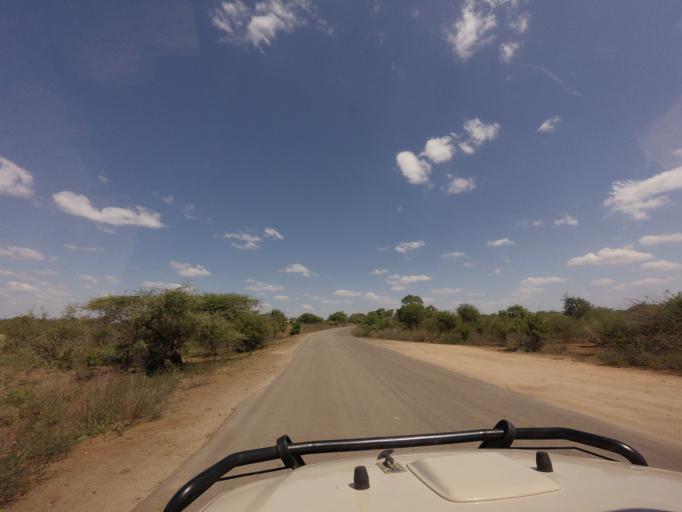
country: ZA
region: Mpumalanga
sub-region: Ehlanzeni District
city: Komatipoort
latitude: -25.1166
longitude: 31.9127
